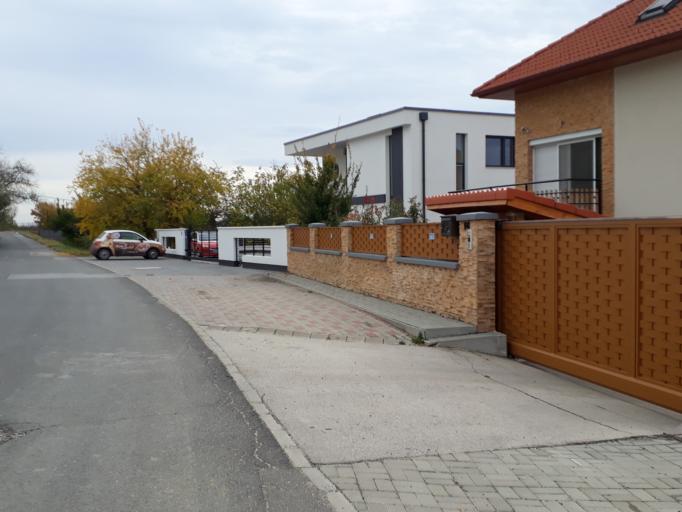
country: HU
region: Budapest
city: Budapest XII. keruelet
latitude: 47.4631
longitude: 19.0014
